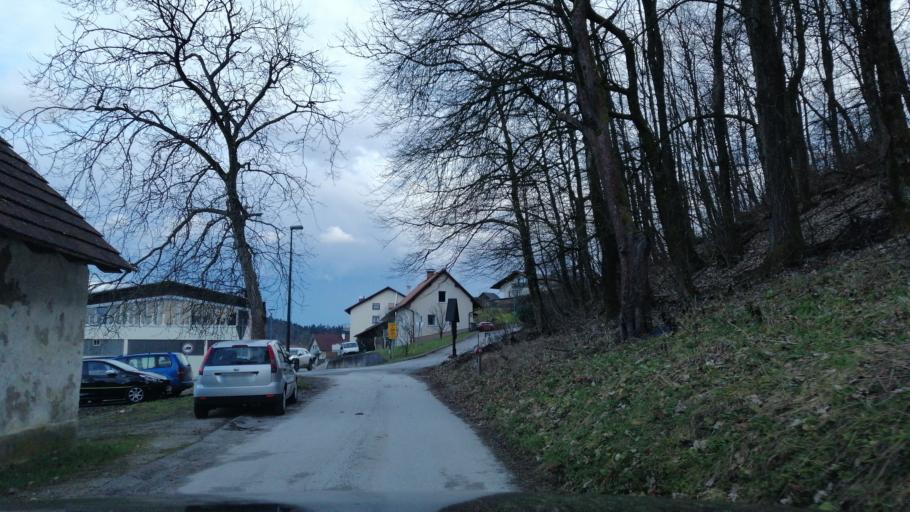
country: SI
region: Medvode
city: Medvode
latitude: 46.1329
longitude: 14.4092
